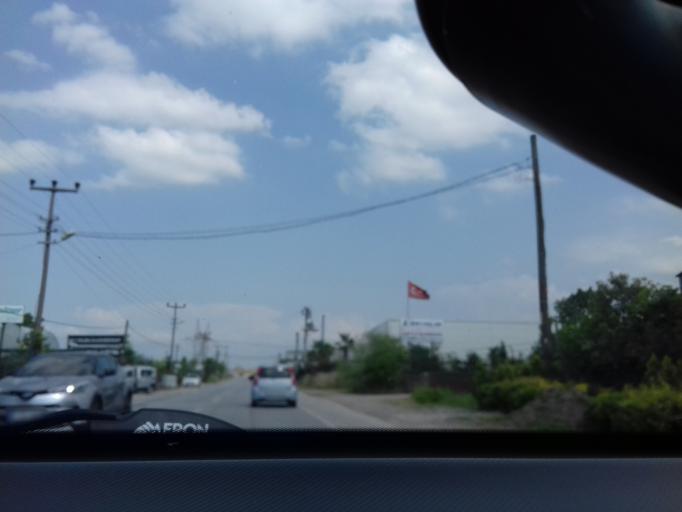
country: TR
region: Sakarya
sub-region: Merkez
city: Sapanca
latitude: 40.7135
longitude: 30.3403
